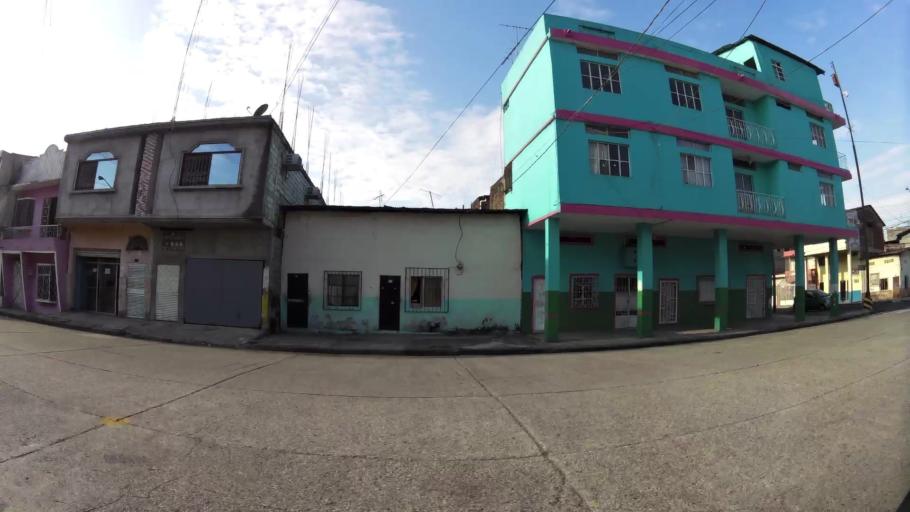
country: EC
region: Guayas
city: Guayaquil
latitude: -2.2096
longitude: -79.9036
